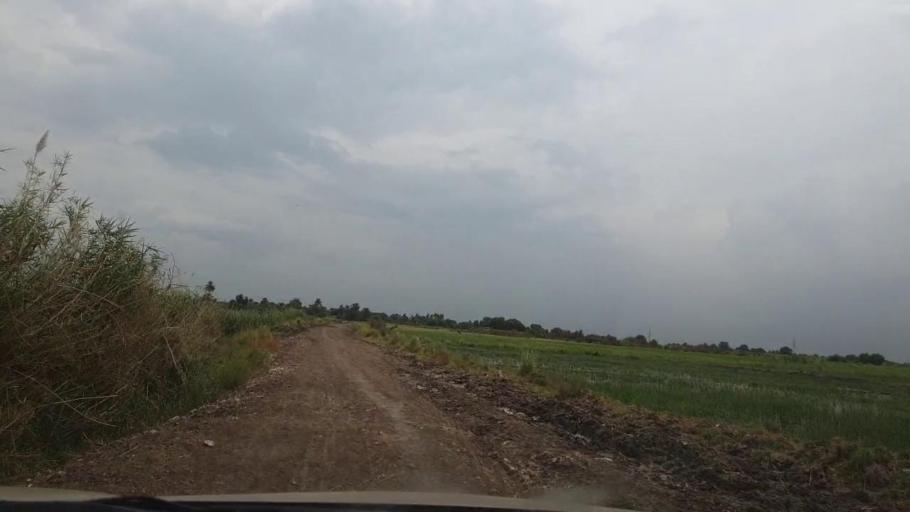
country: PK
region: Sindh
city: Ratodero
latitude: 27.7997
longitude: 68.3132
